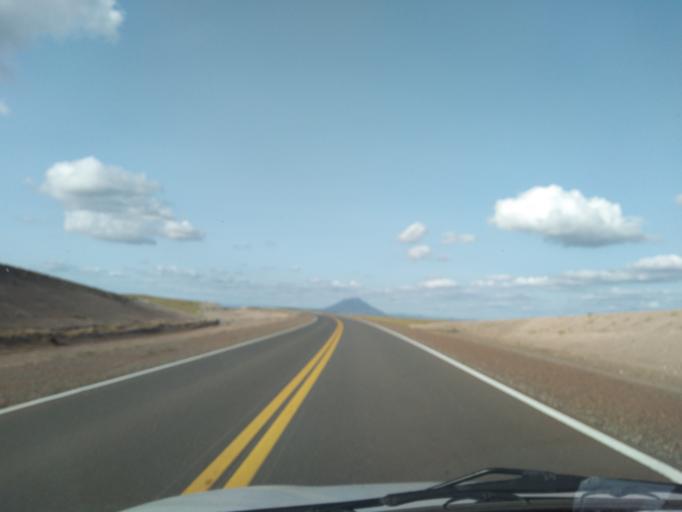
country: AR
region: Mendoza
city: Malargue
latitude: -34.8186
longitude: -69.2496
